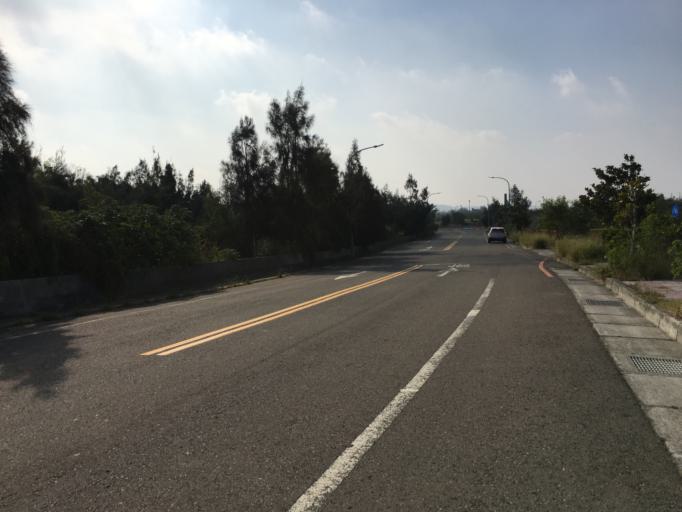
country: TW
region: Taiwan
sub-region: Hsinchu
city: Hsinchu
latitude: 24.8010
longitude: 120.9169
